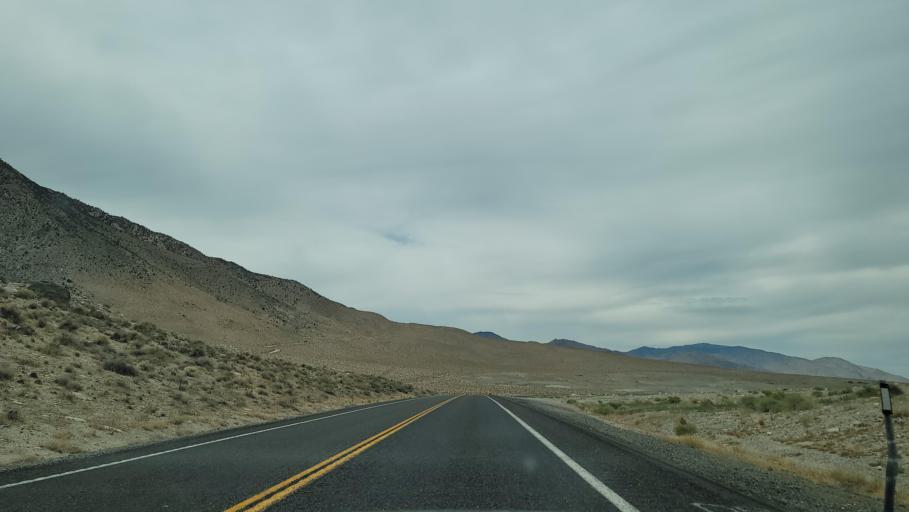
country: US
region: Nevada
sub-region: Mineral County
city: Hawthorne
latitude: 38.5798
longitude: -118.7029
